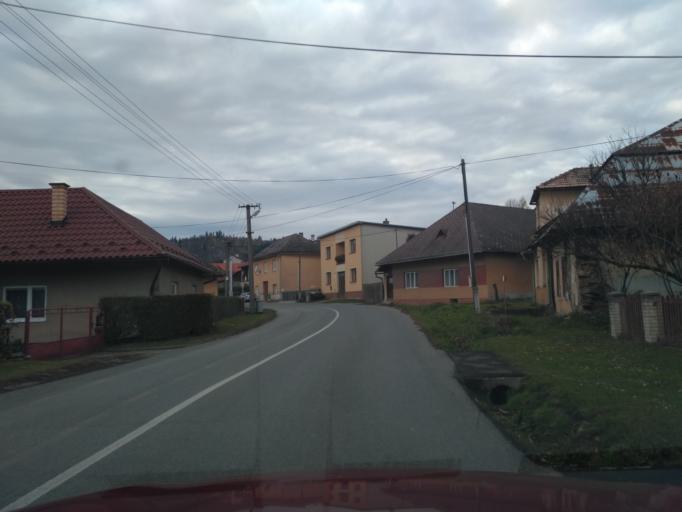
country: SK
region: Presovsky
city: Spisske Podhradie
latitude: 48.8127
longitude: 20.7063
